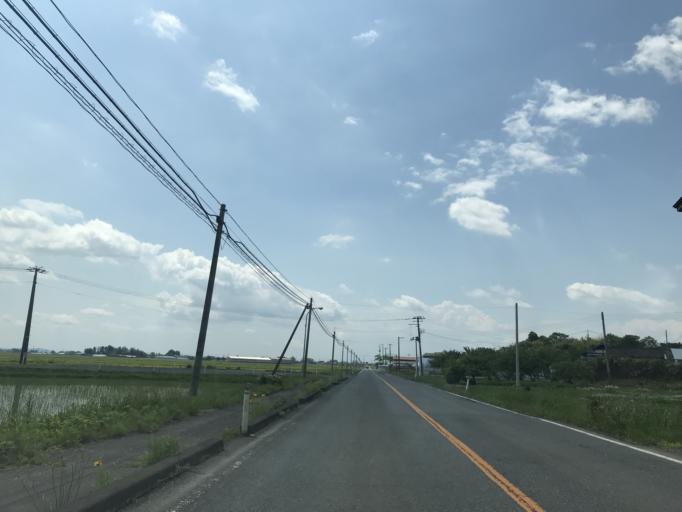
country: JP
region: Miyagi
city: Kogota
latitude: 38.6168
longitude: 141.0193
